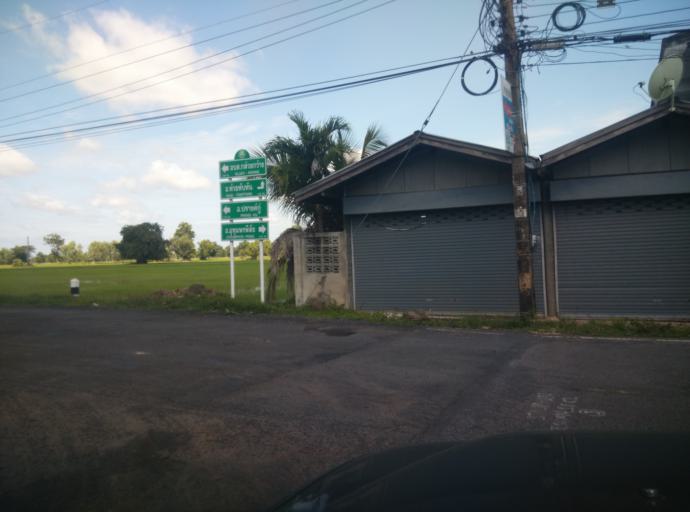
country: TH
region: Sisaket
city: Huai Thap Than
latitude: 14.9826
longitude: 104.0705
